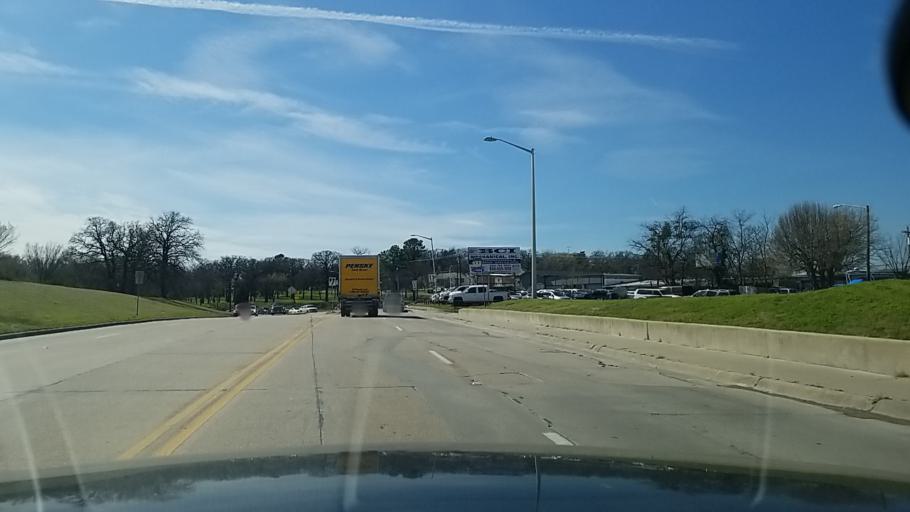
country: US
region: Texas
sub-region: Denton County
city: Denton
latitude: 33.2075
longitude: -97.1311
